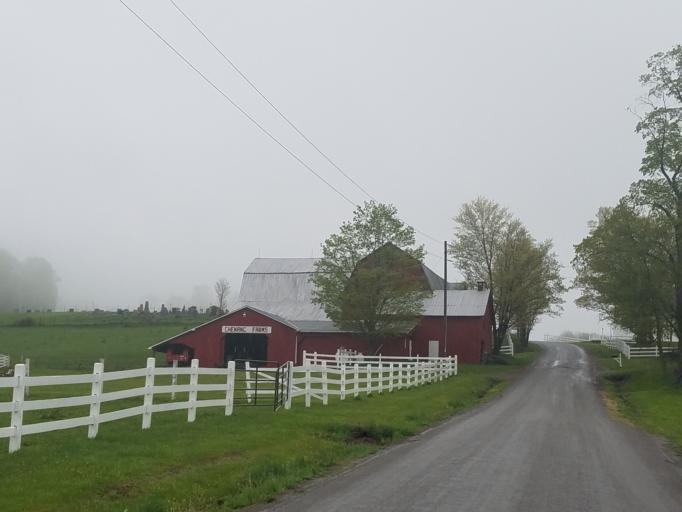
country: US
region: Pennsylvania
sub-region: Tioga County
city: Westfield
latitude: 42.0498
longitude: -77.4680
